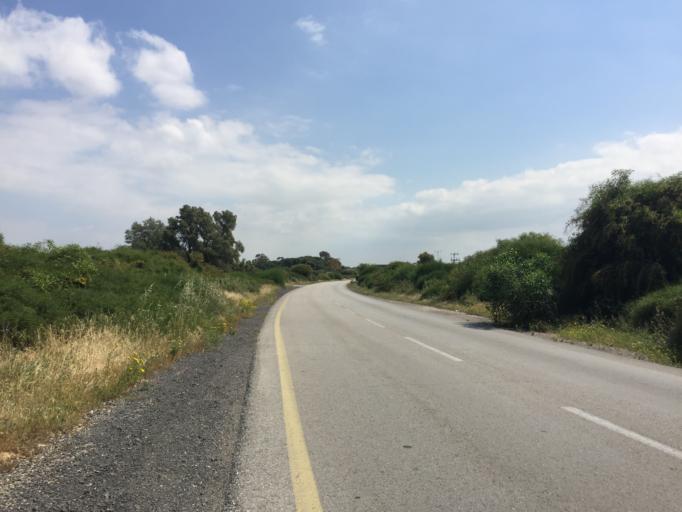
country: IL
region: Haifa
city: Qesarya
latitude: 32.4951
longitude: 34.8962
